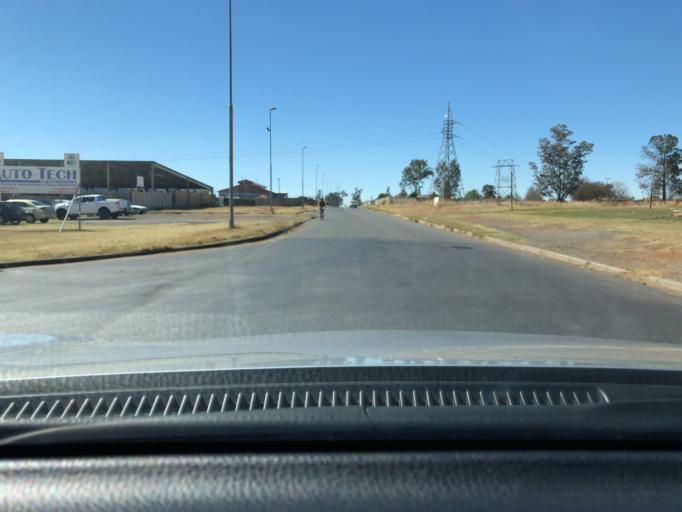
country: ZA
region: KwaZulu-Natal
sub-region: Amajuba District Municipality
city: Newcastle
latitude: -27.7605
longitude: 29.9472
